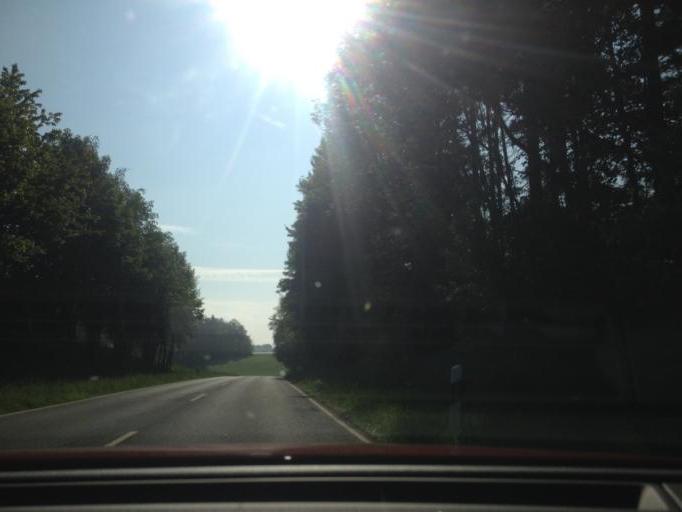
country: DE
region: Bavaria
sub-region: Upper Franconia
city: Pegnitz
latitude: 49.7608
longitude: 11.5742
